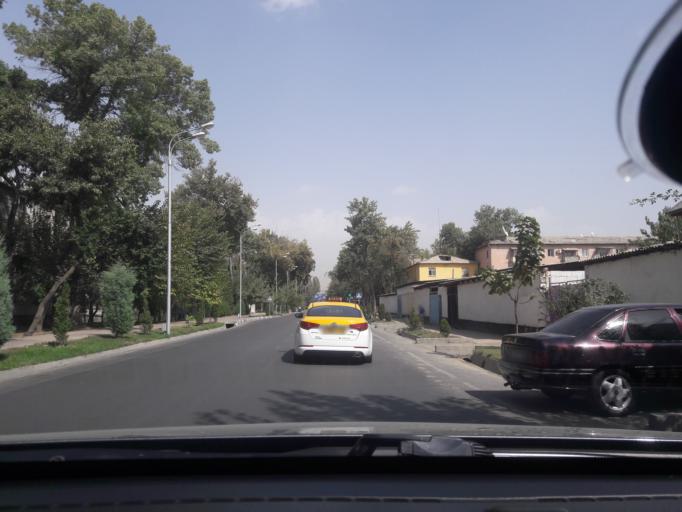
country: TJ
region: Dushanbe
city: Dushanbe
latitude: 38.5650
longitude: 68.7631
